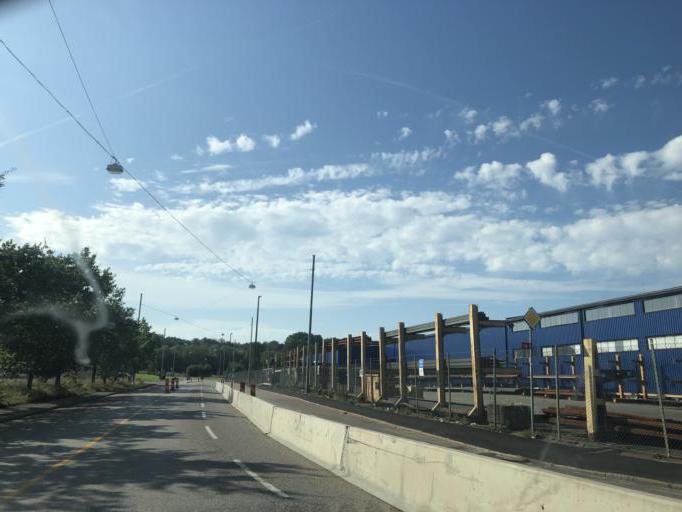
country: SE
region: Vaestra Goetaland
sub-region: Goteborg
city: Goeteborg
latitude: 57.7377
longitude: 11.9930
